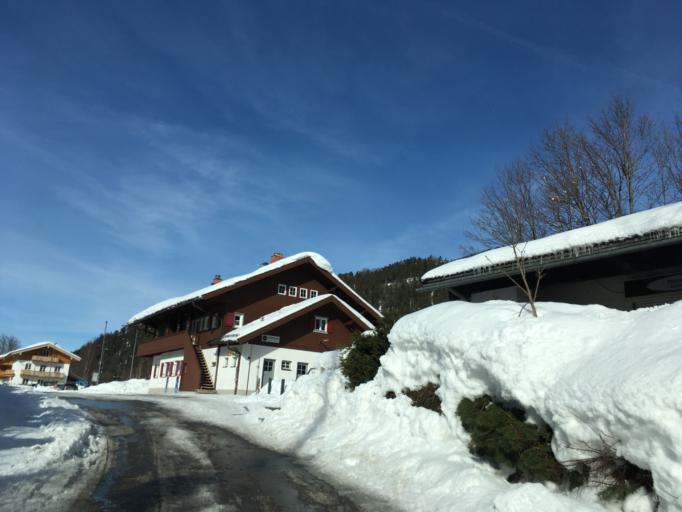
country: DE
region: Bavaria
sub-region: Upper Bavaria
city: Bayrischzell
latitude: 47.6748
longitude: 12.0120
